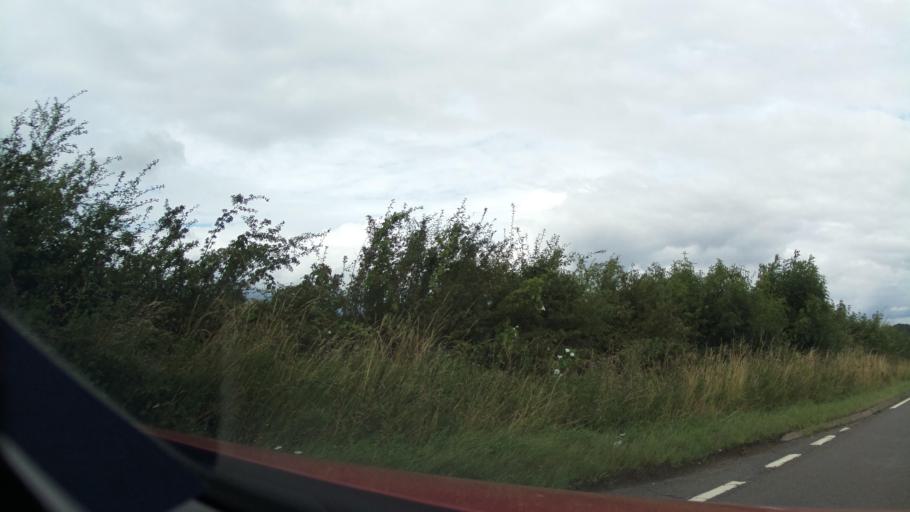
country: GB
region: England
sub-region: Northamptonshire
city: Corby
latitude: 52.4905
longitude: -0.7325
